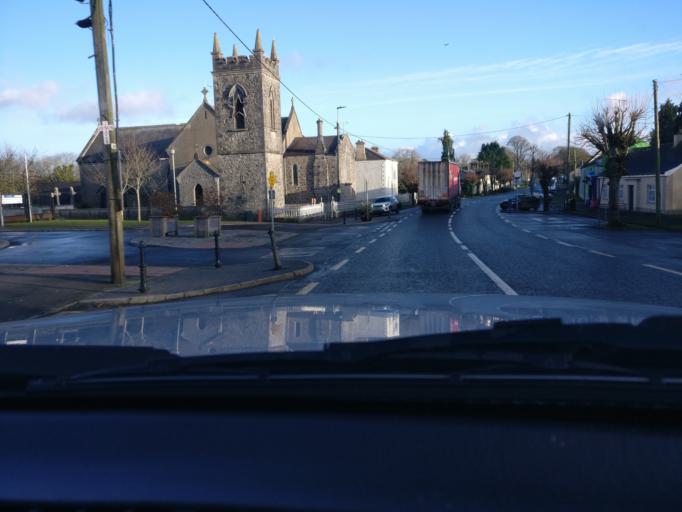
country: IE
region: Leinster
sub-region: An Mhi
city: Athboy
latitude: 53.6636
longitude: -7.0146
